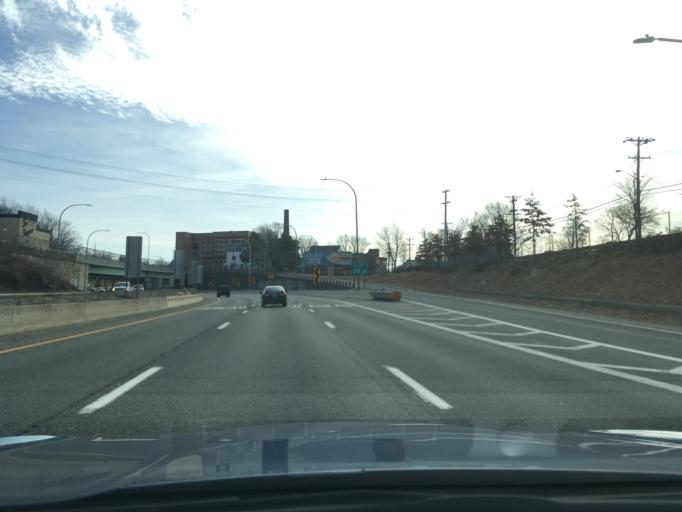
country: US
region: Rhode Island
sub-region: Providence County
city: Pawtucket
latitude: 41.8851
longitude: -71.3787
